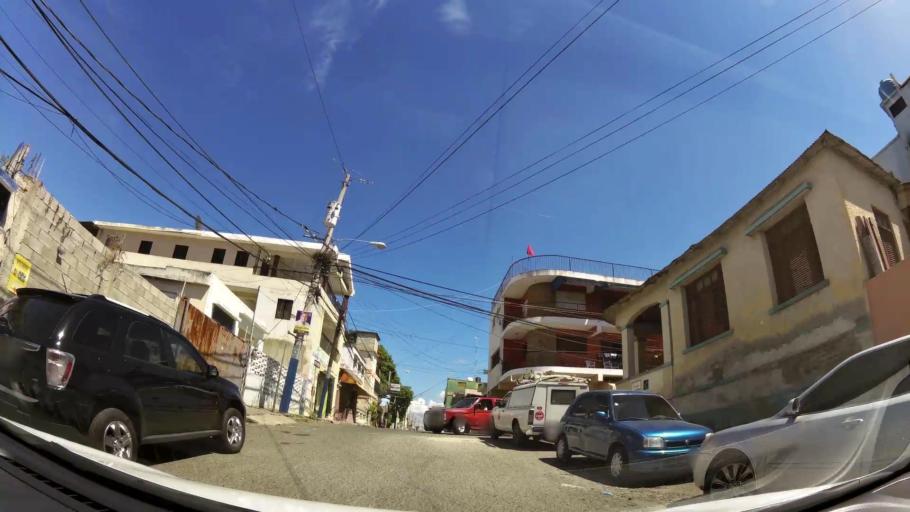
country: DO
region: Santiago
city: Santiago de los Caballeros
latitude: 19.4526
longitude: -70.7087
